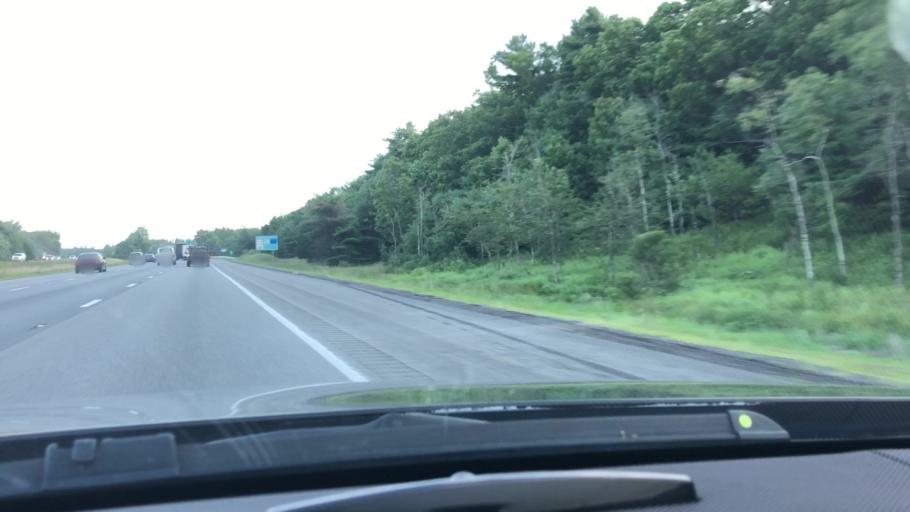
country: US
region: Massachusetts
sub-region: Norfolk County
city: Franklin
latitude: 42.0831
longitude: -71.4224
